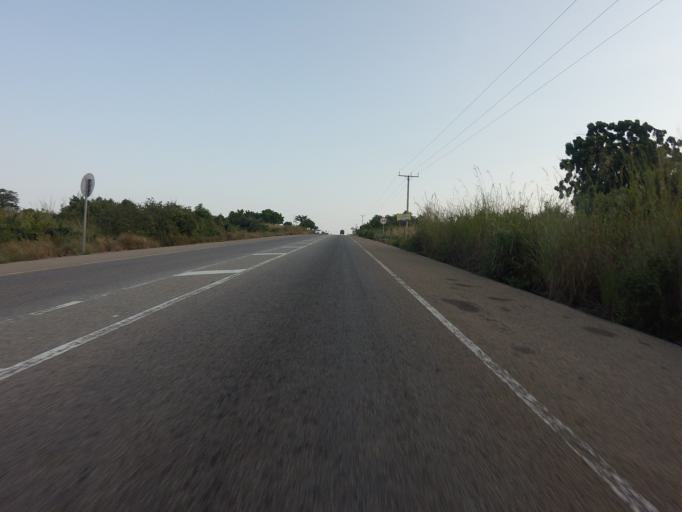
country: GH
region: Volta
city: Anloga
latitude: 6.0410
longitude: 0.6047
